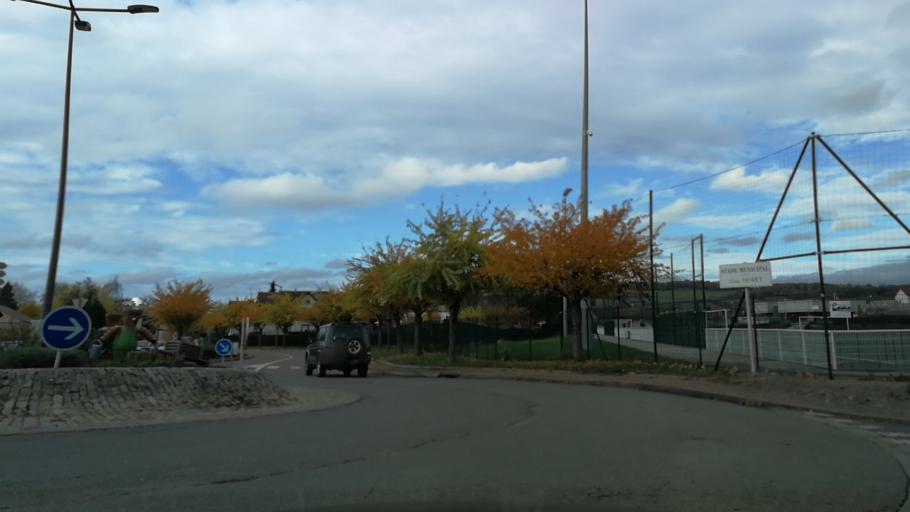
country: FR
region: Bourgogne
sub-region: Departement de la Cote-d'Or
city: Pouilly-en-Auxois
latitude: 47.2688
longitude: 4.5470
